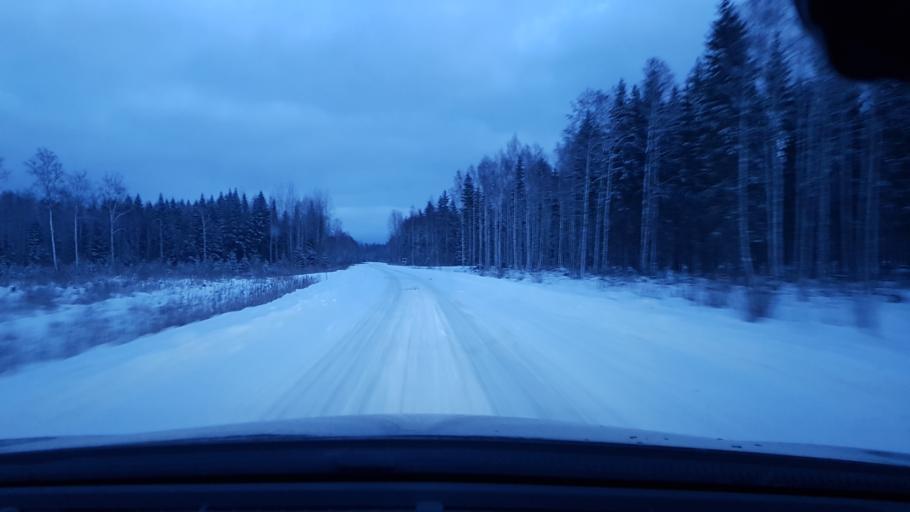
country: EE
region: Harju
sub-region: Nissi vald
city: Turba
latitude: 59.1267
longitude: 24.0833
